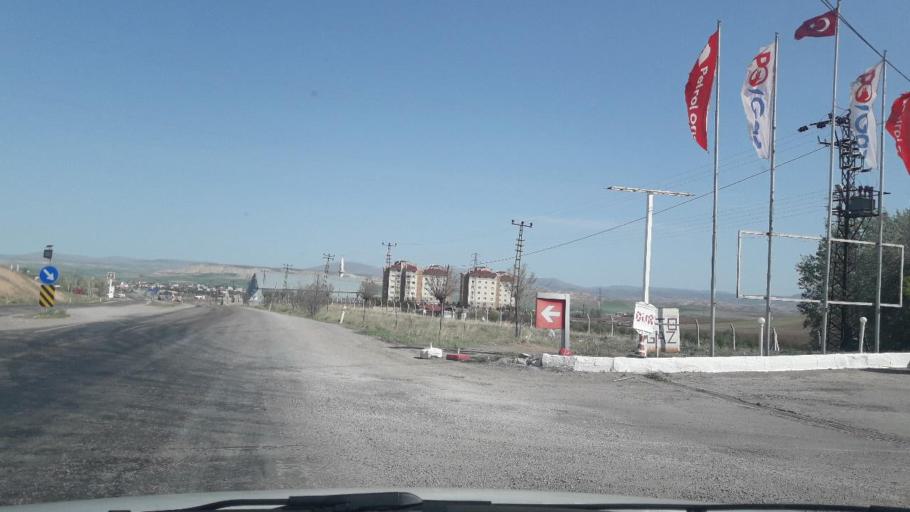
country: TR
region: Sivas
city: Kangal
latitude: 39.2203
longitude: 37.4060
